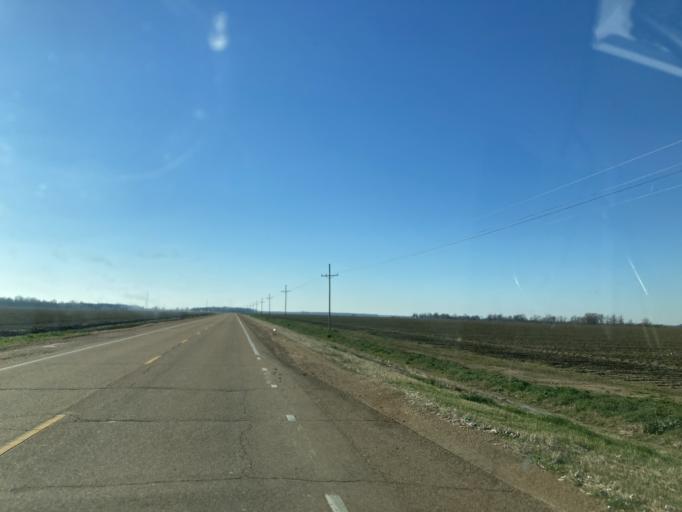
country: US
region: Mississippi
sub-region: Yazoo County
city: Yazoo City
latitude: 32.9518
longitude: -90.5846
